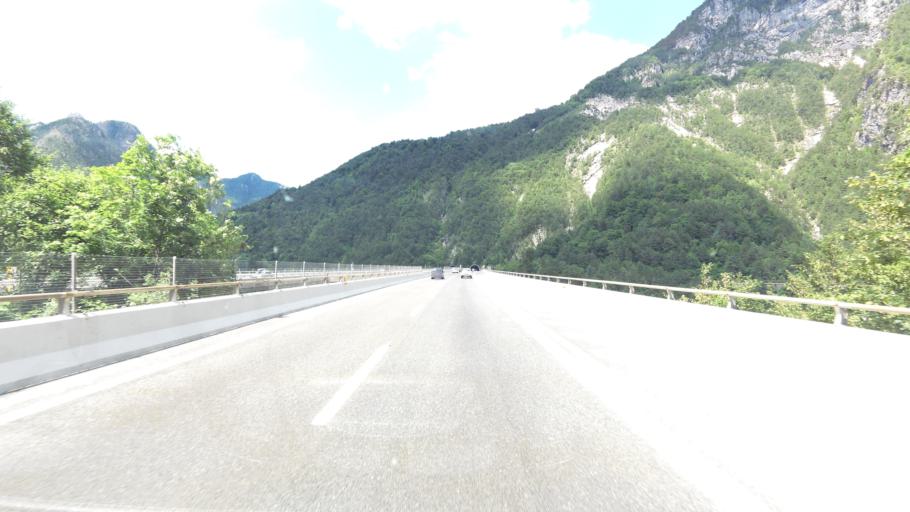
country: IT
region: Friuli Venezia Giulia
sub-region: Provincia di Udine
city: Dogna
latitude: 46.4496
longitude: 13.3057
